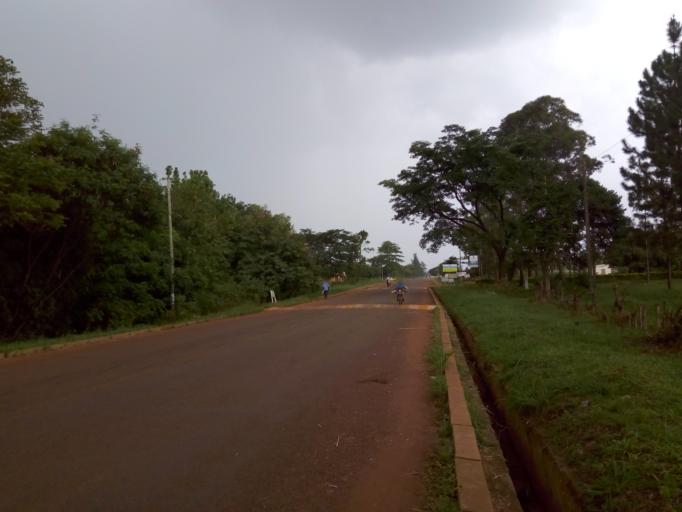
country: UG
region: Western Region
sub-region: Masindi District
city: Masindi
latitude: 1.6849
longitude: 31.7048
